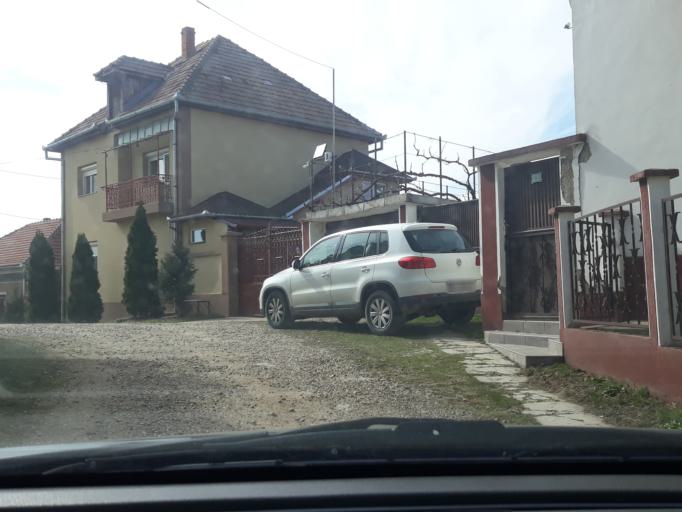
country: RO
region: Bihor
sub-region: Comuna Paleu
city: Paleu
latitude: 47.1147
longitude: 21.9570
